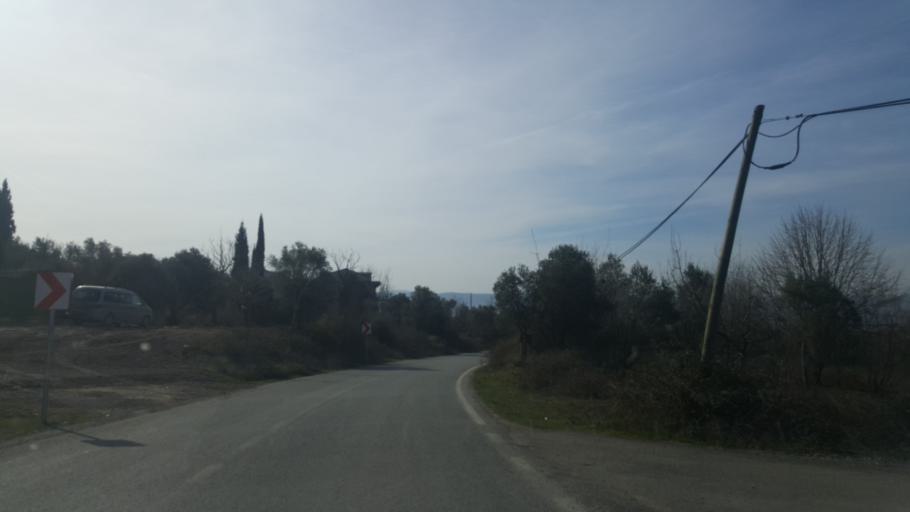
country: TR
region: Kocaeli
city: Tavsancil
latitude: 40.7803
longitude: 29.5749
